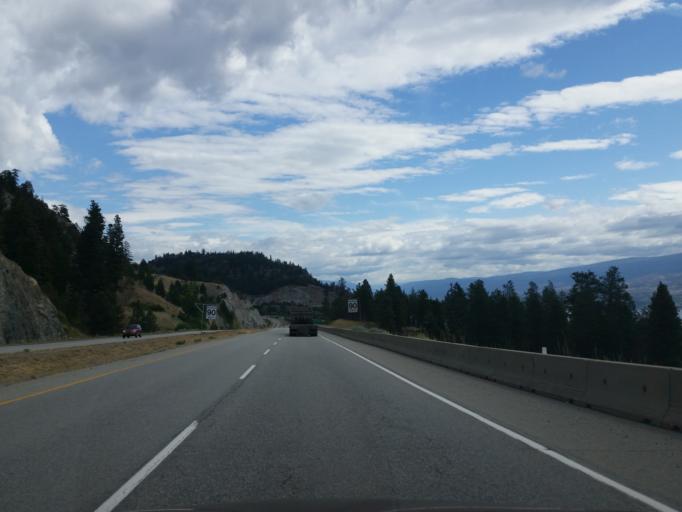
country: CA
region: British Columbia
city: Peachland
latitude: 49.8026
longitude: -119.6774
